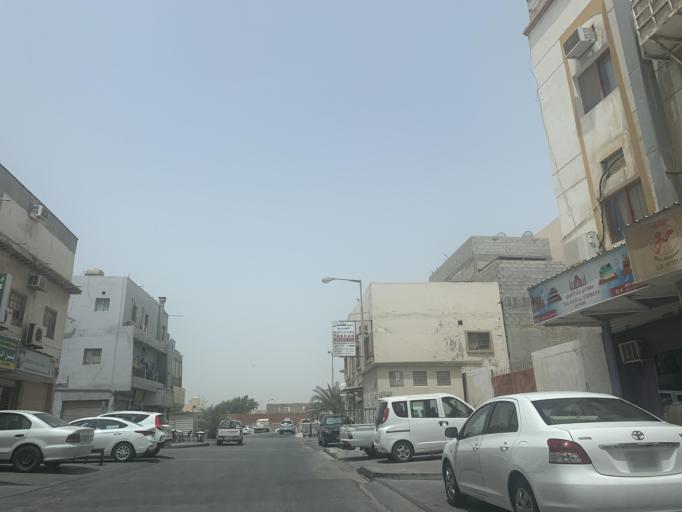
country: BH
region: Manama
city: Jidd Hafs
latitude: 26.2088
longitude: 50.5463
